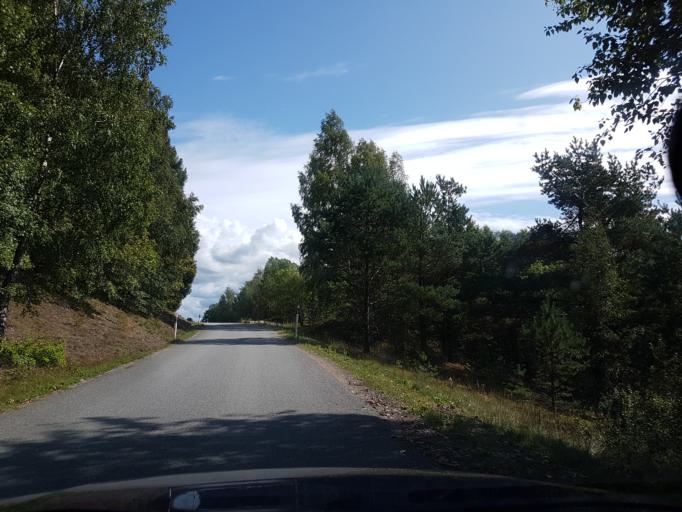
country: SE
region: Vaestra Goetaland
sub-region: Lerums Kommun
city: Grabo
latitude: 57.8468
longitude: 12.3146
